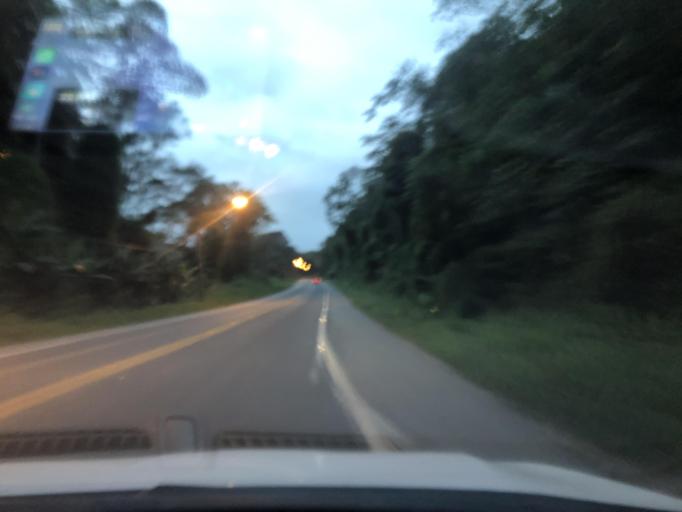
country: BR
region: Santa Catarina
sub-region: Pomerode
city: Pomerode
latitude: -26.7315
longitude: -49.0638
